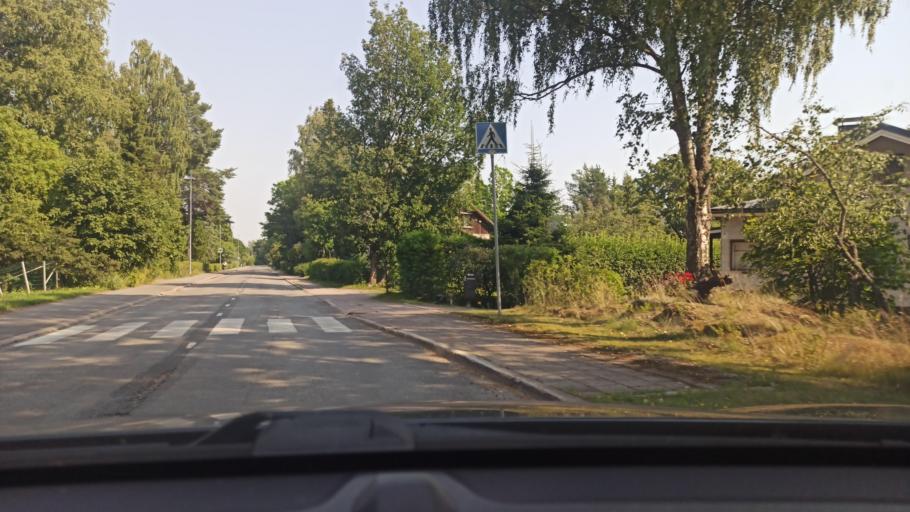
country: FI
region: Varsinais-Suomi
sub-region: Turku
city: Turku
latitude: 60.4610
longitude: 22.2256
